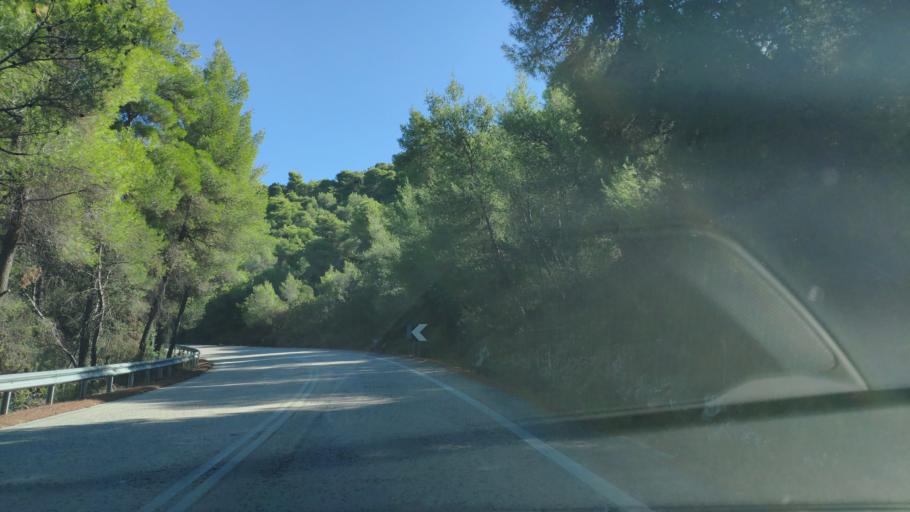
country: GR
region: Peloponnese
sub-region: Nomos Korinthias
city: Sofikon
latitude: 37.8275
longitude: 23.0438
